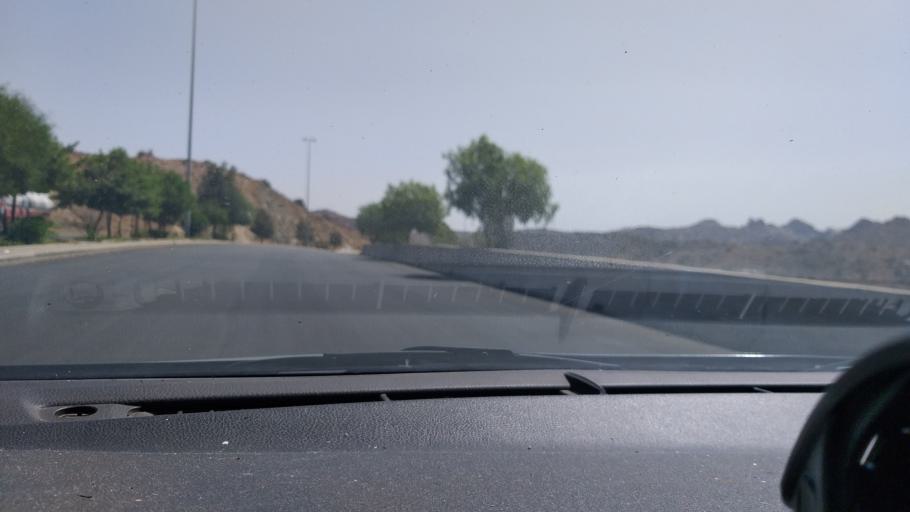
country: SA
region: Makkah
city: Ash Shafa
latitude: 21.0953
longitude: 40.3215
